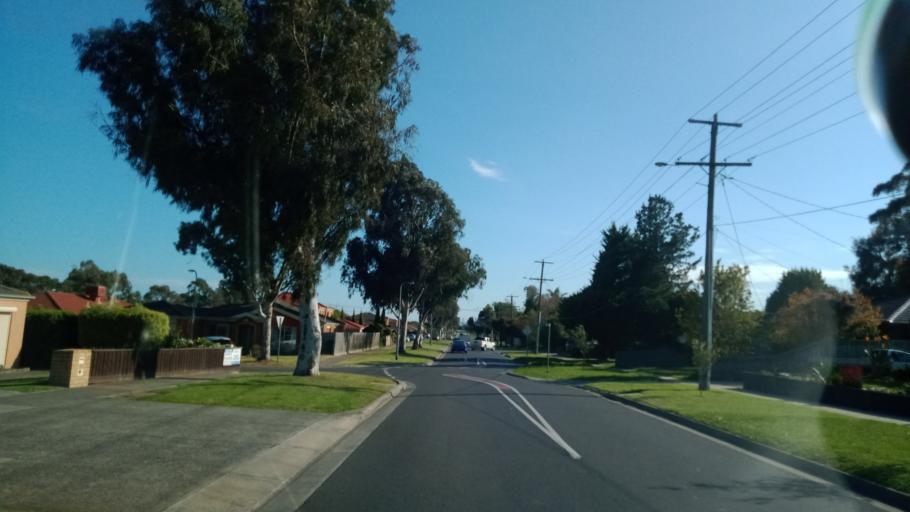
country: AU
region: Victoria
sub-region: Casey
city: Cranbourne West
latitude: -38.0946
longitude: 145.2682
